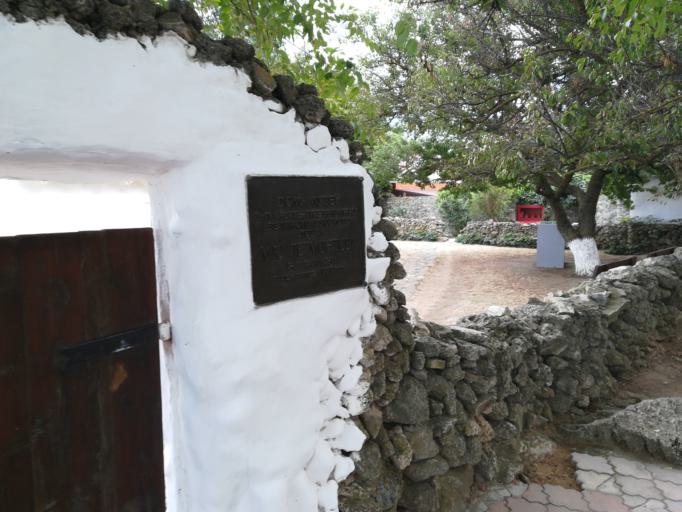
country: RU
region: Krasnodarskiy
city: Taman'
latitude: 45.2182
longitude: 36.7251
